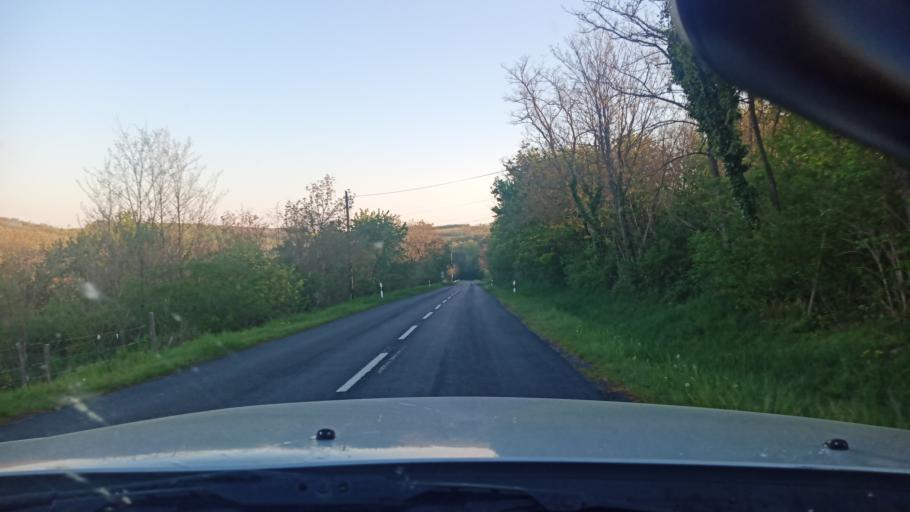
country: HU
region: Zala
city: Heviz
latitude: 46.7858
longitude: 17.1451
